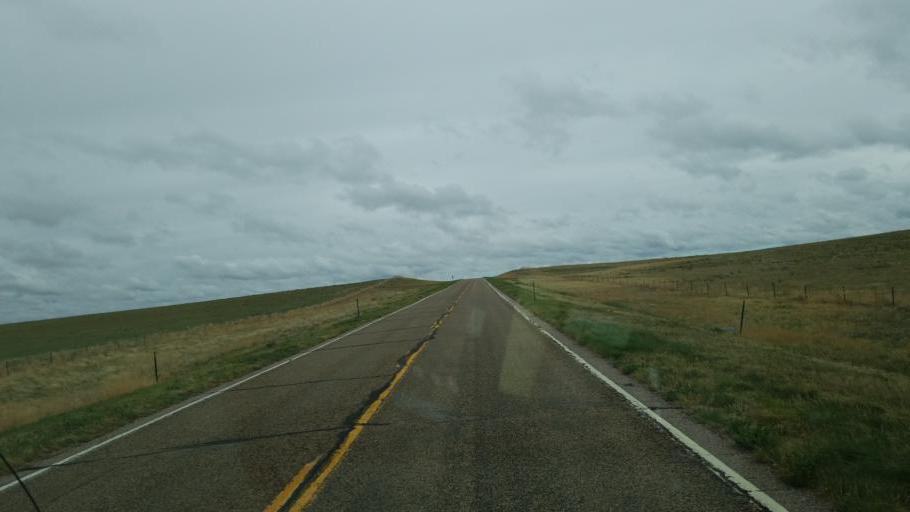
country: US
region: Colorado
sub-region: Lincoln County
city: Hugo
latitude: 38.8503
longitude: -103.4496
